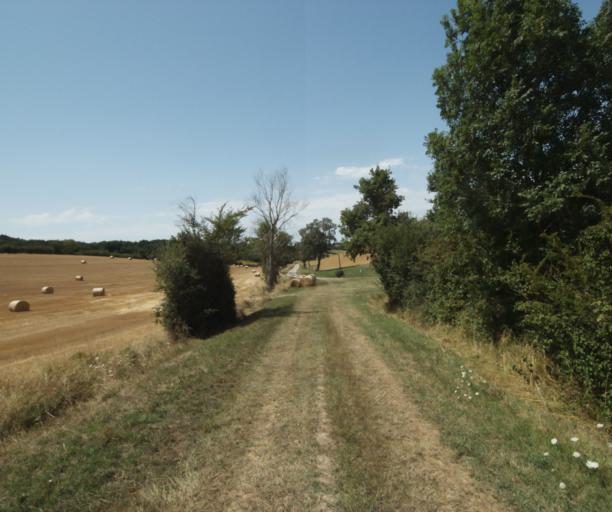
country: FR
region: Midi-Pyrenees
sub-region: Departement de la Haute-Garonne
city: Saint-Felix-Lauragais
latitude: 43.4440
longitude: 1.8725
